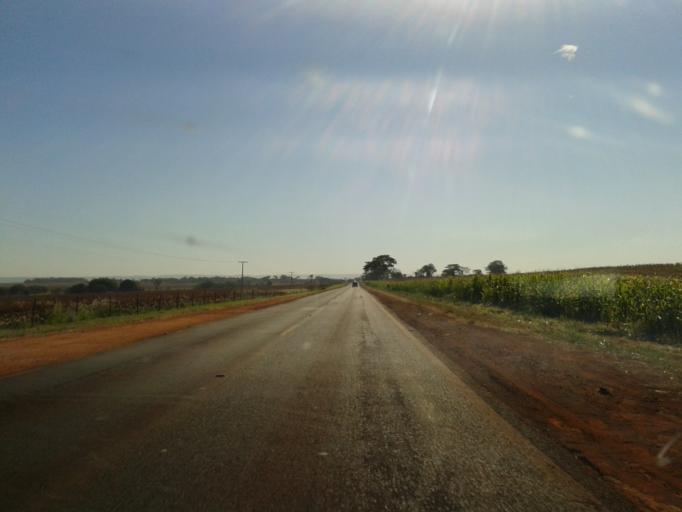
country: BR
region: Minas Gerais
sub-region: Capinopolis
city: Capinopolis
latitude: -18.6130
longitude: -49.5292
